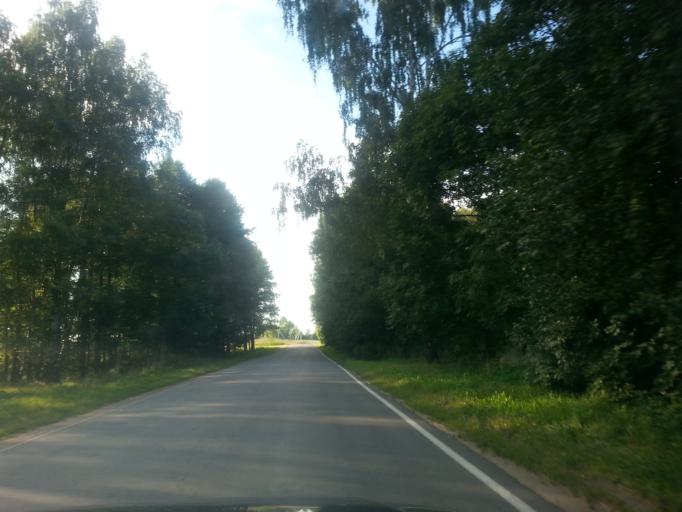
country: BY
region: Minsk
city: Narach
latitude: 54.9640
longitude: 26.6422
